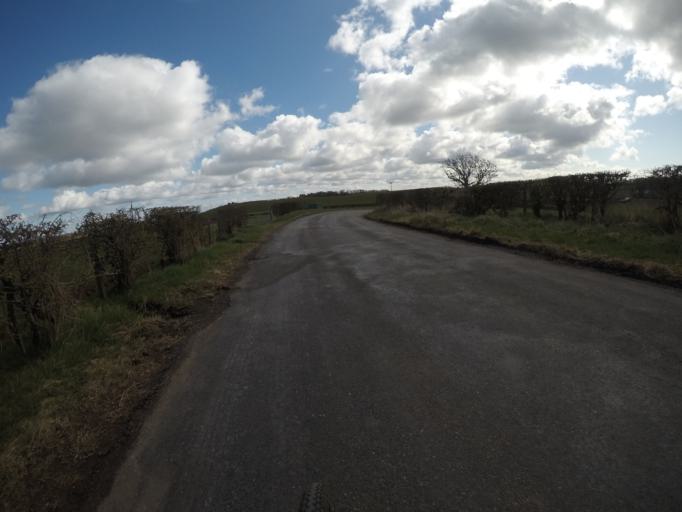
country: GB
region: Scotland
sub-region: South Ayrshire
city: Dundonald
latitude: 55.5899
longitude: -4.5791
